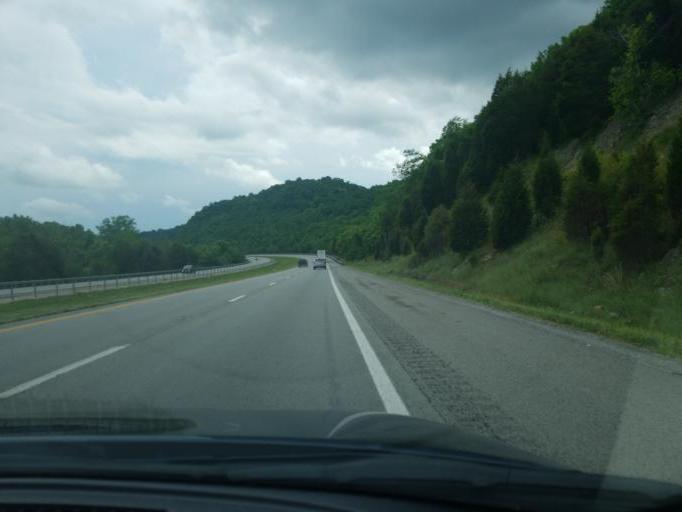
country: US
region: Kentucky
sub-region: Trimble County
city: Providence
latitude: 38.6129
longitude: -85.1648
